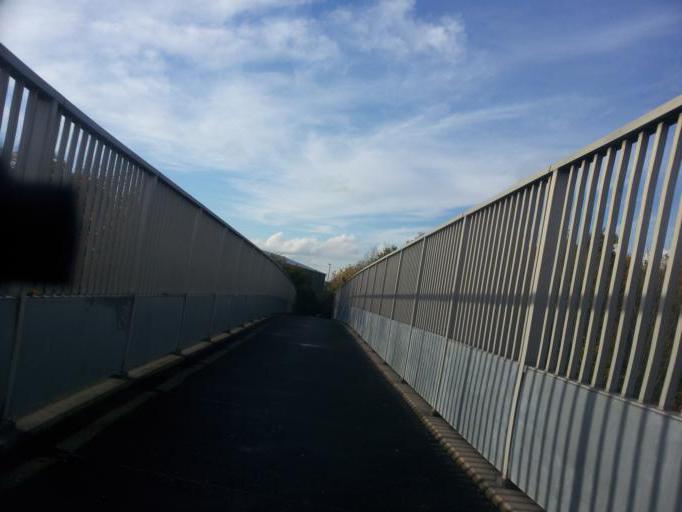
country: GB
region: England
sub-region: Kent
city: Sittingbourne
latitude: 51.3627
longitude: 0.7279
